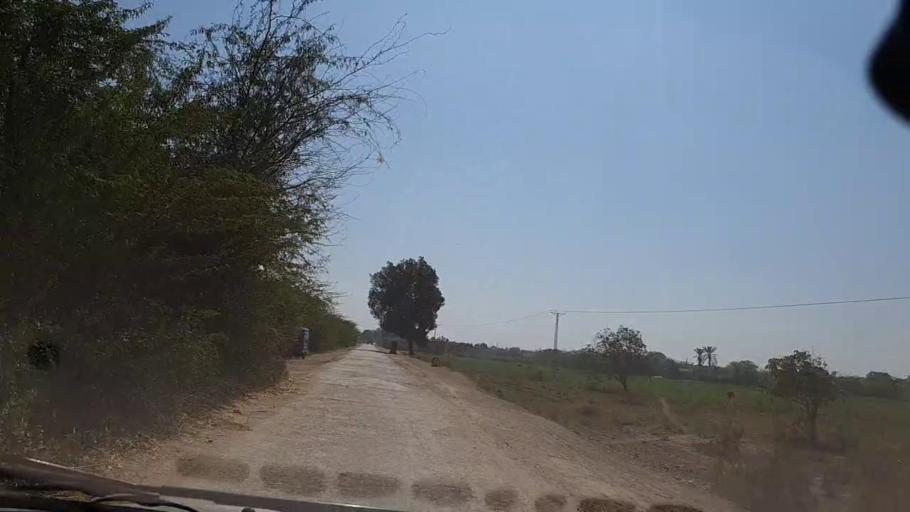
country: PK
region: Sindh
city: Mirpur Khas
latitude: 25.4790
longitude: 69.0474
